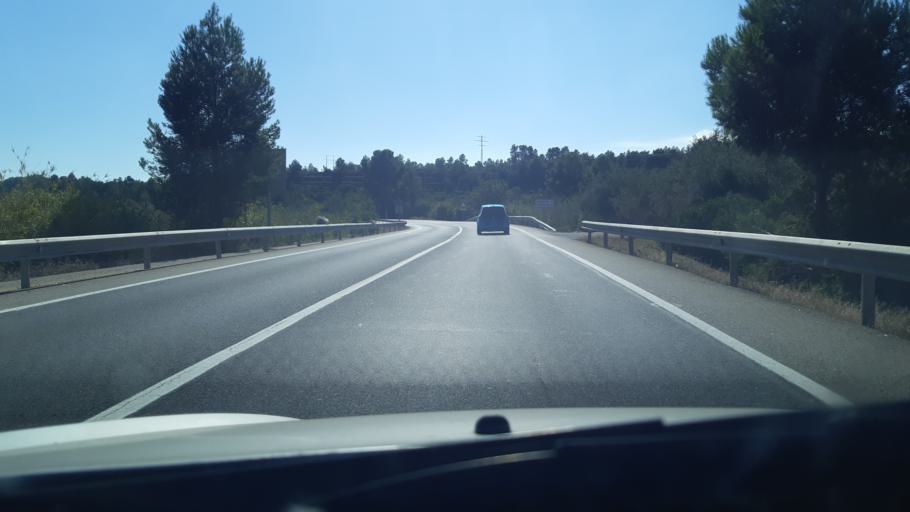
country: ES
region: Catalonia
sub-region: Provincia de Tarragona
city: Tivenys
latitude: 40.9033
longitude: 0.4831
